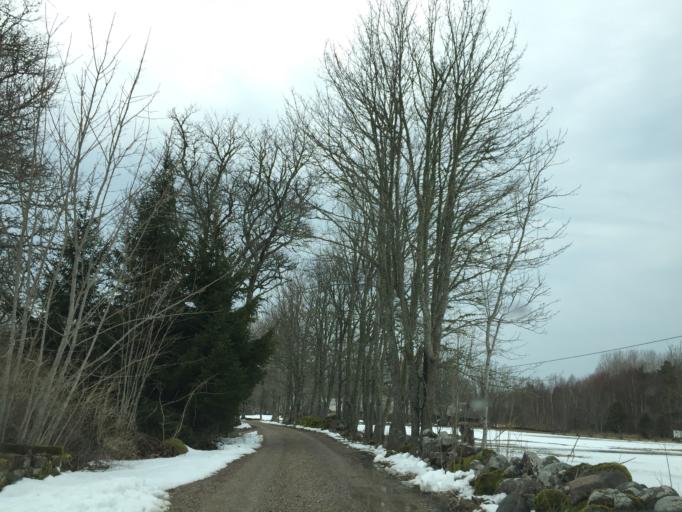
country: EE
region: Saare
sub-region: Kuressaare linn
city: Kuressaare
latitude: 58.4404
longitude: 22.1436
